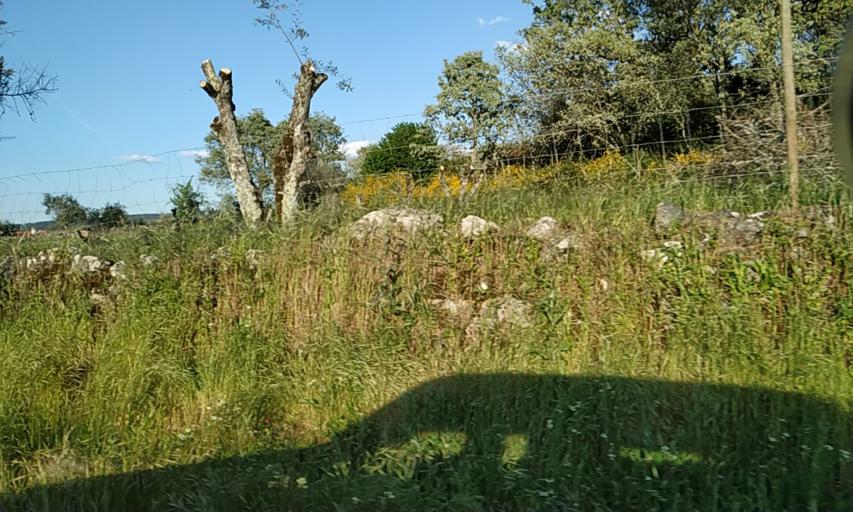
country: PT
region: Portalegre
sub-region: Marvao
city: Marvao
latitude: 39.3573
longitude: -7.4064
